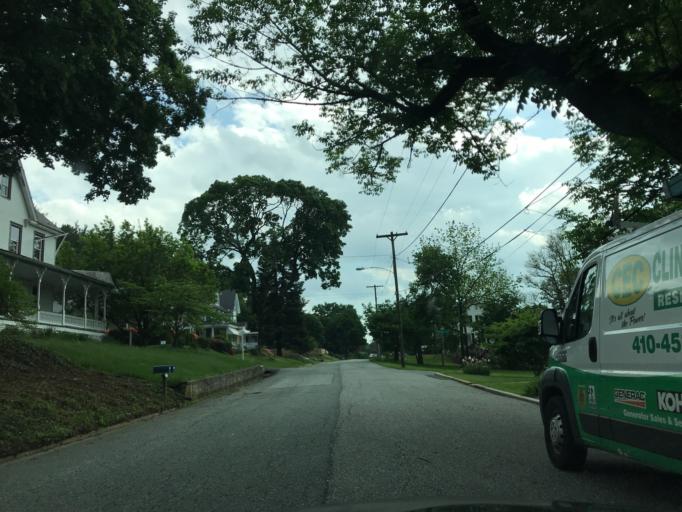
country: US
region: Pennsylvania
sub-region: York County
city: Susquehanna Trails
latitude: 39.7200
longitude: -76.3346
